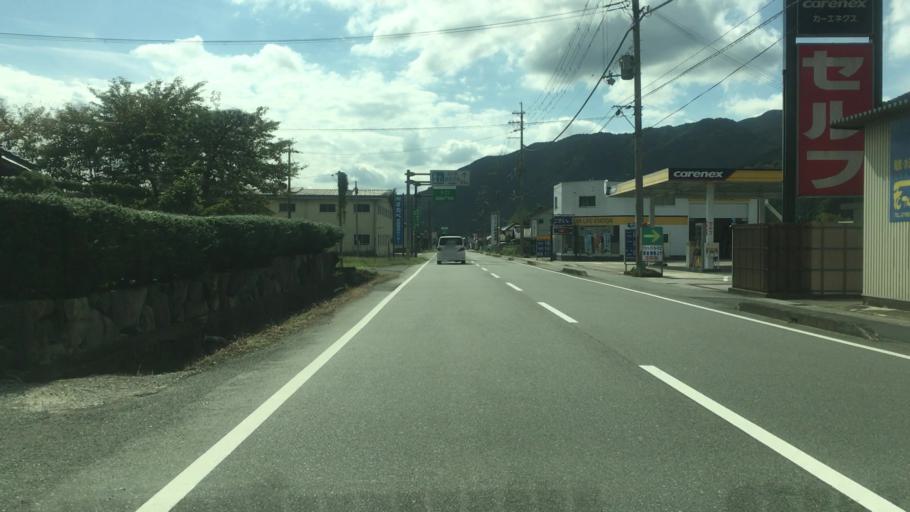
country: JP
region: Kyoto
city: Fukuchiyama
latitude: 35.2460
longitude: 135.0069
